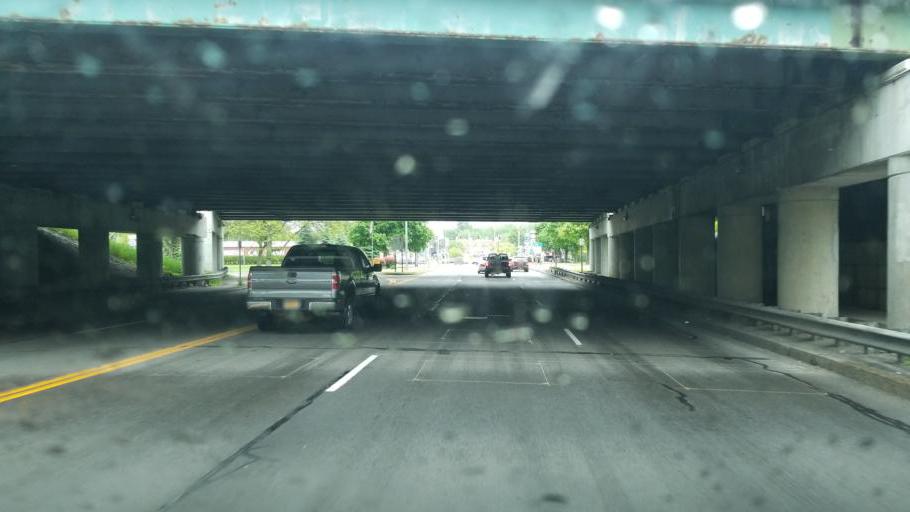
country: US
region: New York
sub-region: Oneida County
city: Utica
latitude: 43.1147
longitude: -75.2125
